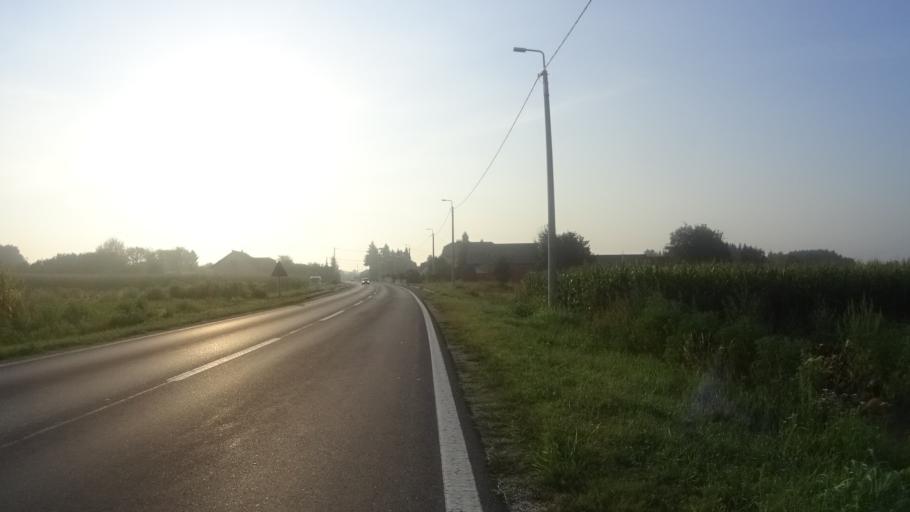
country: HR
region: Varazdinska
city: Petrijanec
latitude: 46.3483
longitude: 16.2101
